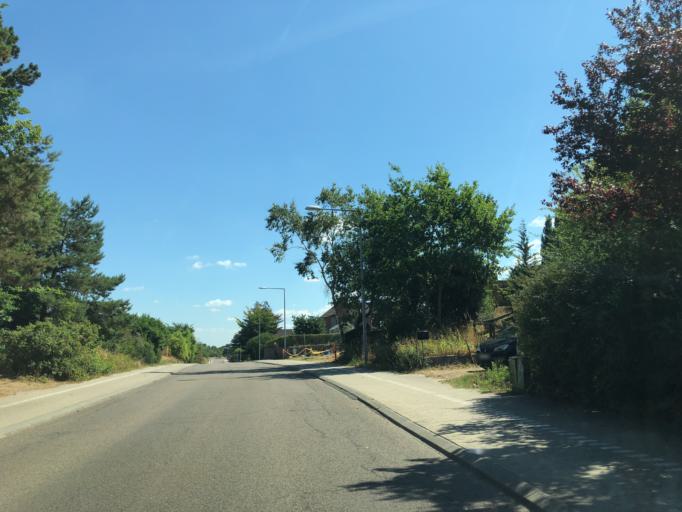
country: DK
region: Capital Region
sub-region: Halsnaes Kommune
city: Hundested
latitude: 55.9535
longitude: 11.8615
